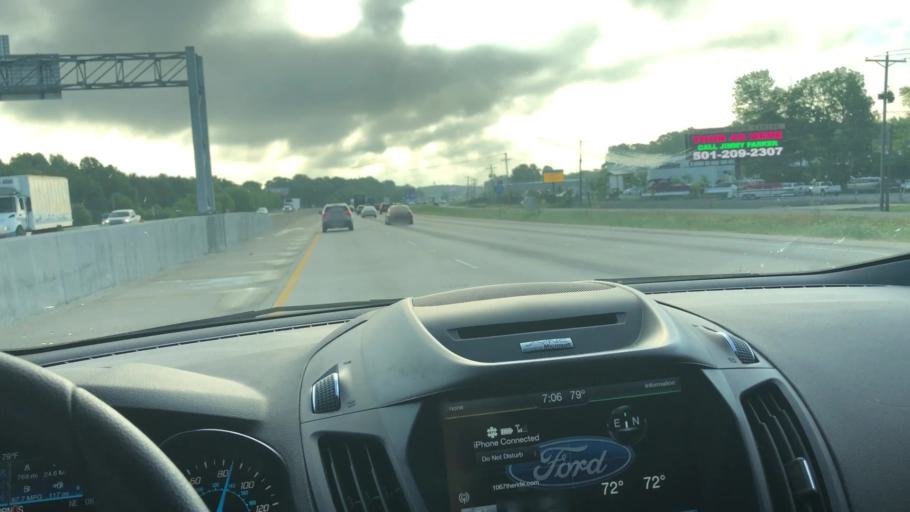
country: US
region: Arkansas
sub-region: Pulaski County
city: Alexander
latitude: 34.6443
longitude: -92.4352
